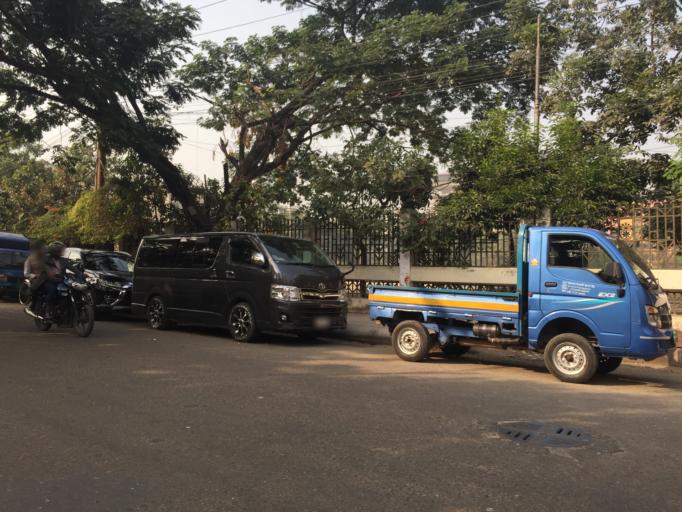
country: BD
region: Dhaka
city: Paltan
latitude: 23.7336
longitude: 90.4058
